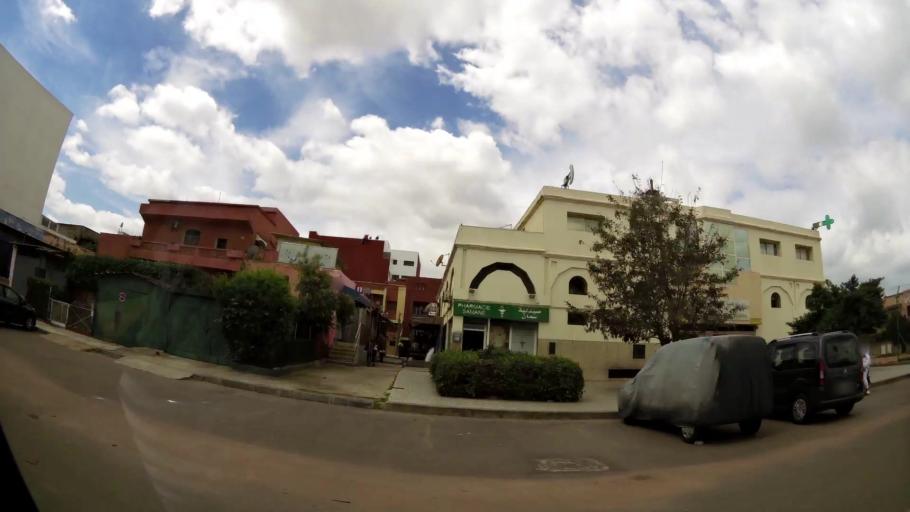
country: MA
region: Grand Casablanca
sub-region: Casablanca
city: Casablanca
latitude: 33.6136
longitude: -7.5460
